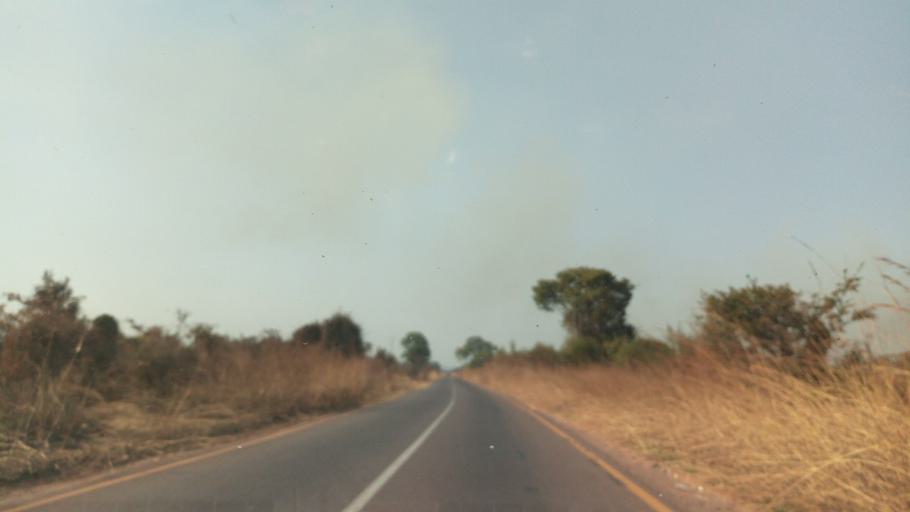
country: CD
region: Katanga
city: Lubumbashi
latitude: -11.4172
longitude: 27.7376
